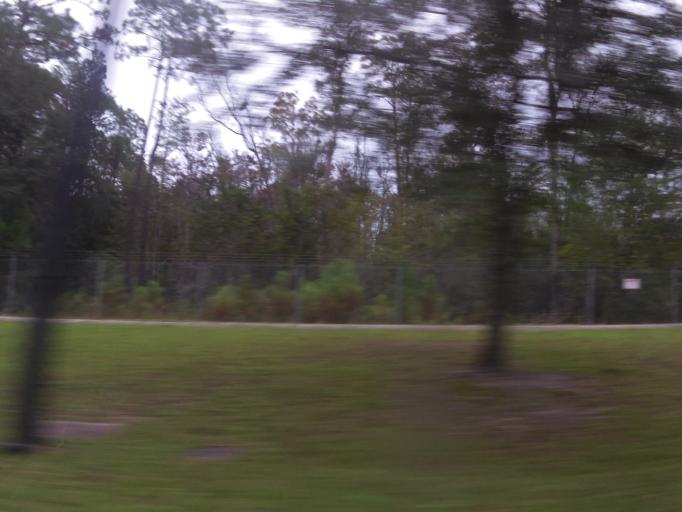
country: US
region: Florida
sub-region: Duval County
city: Baldwin
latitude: 30.2443
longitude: -81.8831
